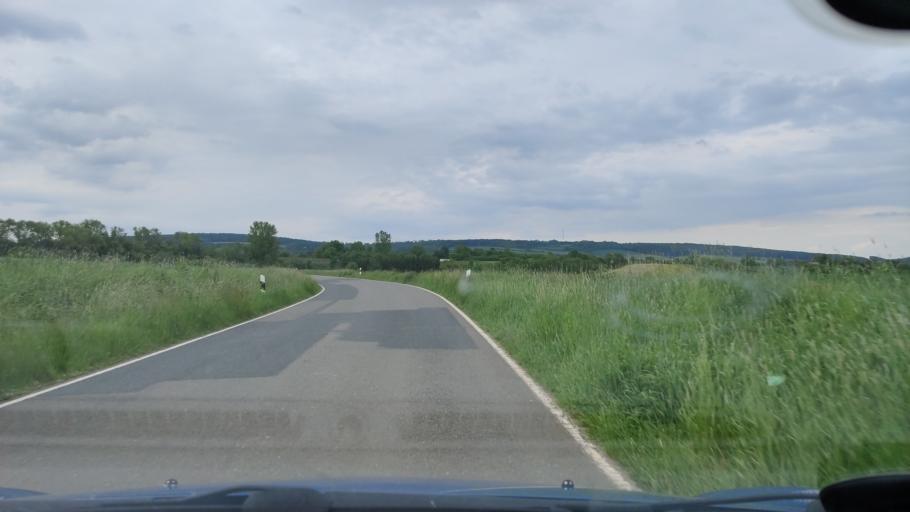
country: DE
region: Lower Saxony
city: Freden
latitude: 51.8841
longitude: 9.8536
